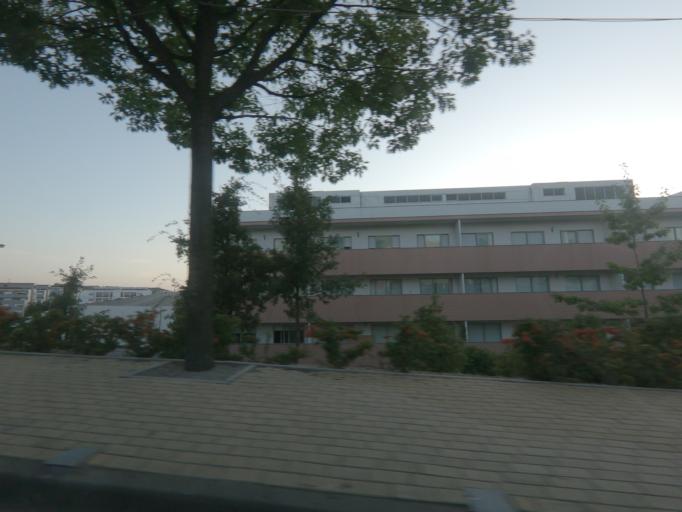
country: PT
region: Vila Real
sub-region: Vila Real
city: Vila Real
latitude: 41.2974
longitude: -7.7322
